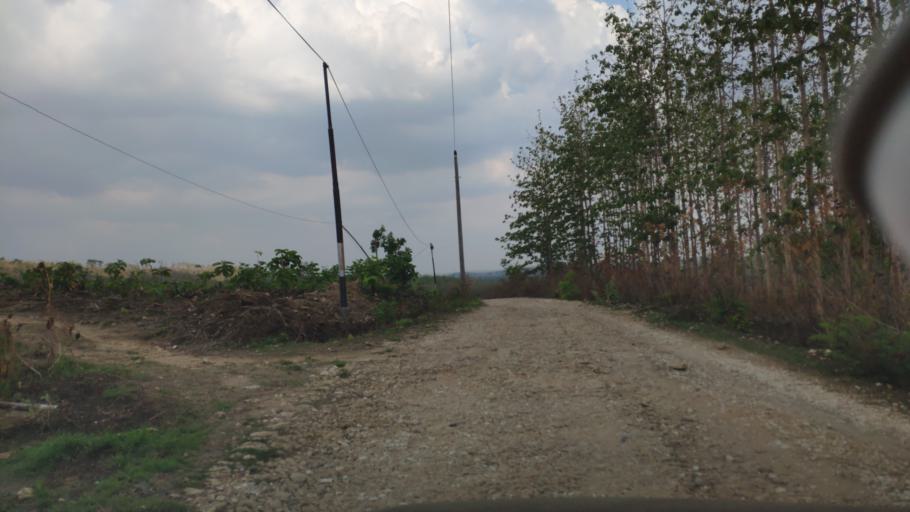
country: ID
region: Central Java
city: Semanggi
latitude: -7.0636
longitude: 111.4180
